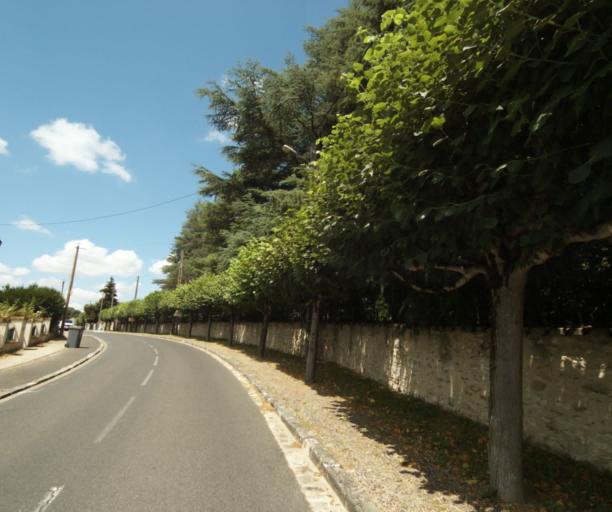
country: FR
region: Ile-de-France
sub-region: Departement de Seine-et-Marne
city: Chartrettes
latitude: 48.4866
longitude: 2.7087
